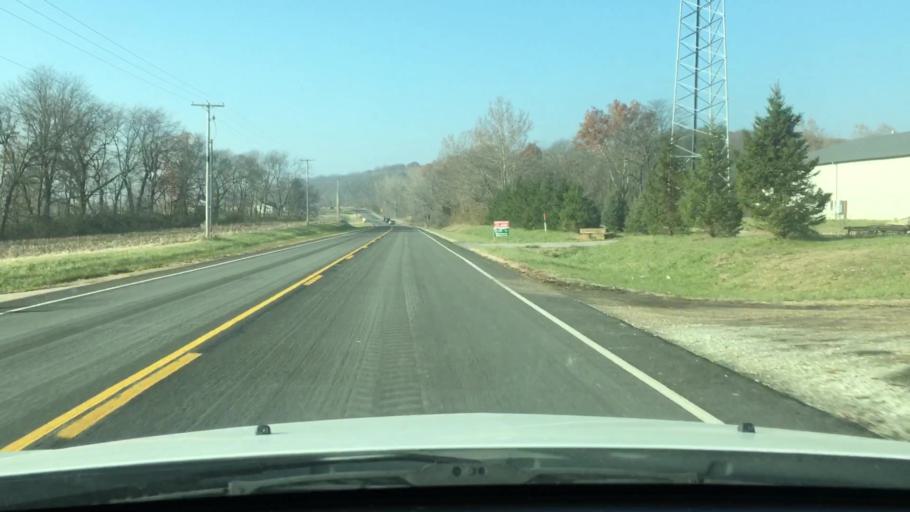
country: US
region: Illinois
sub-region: Mason County
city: Havana
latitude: 40.4197
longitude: -90.0043
